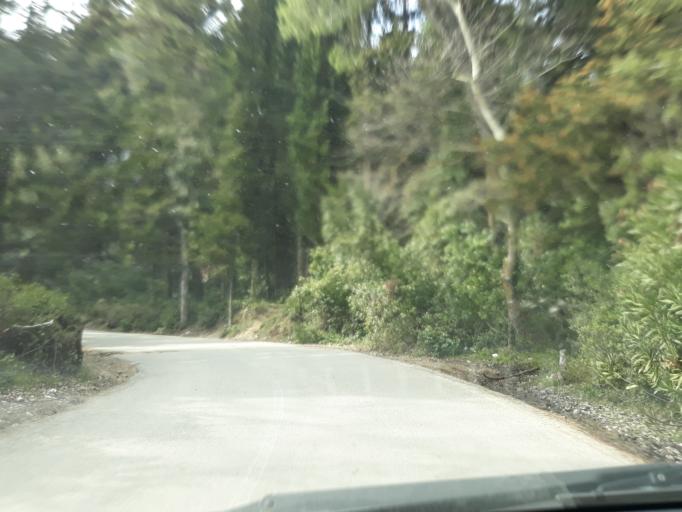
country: GR
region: Attica
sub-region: Nomarchia Anatolikis Attikis
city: Varybobi
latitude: 38.1609
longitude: 23.7923
